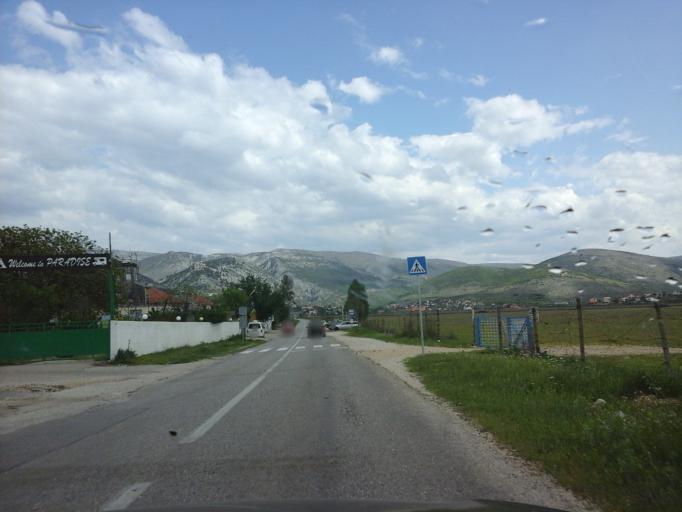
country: BA
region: Federation of Bosnia and Herzegovina
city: Blagaj
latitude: 43.2691
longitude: 17.8636
